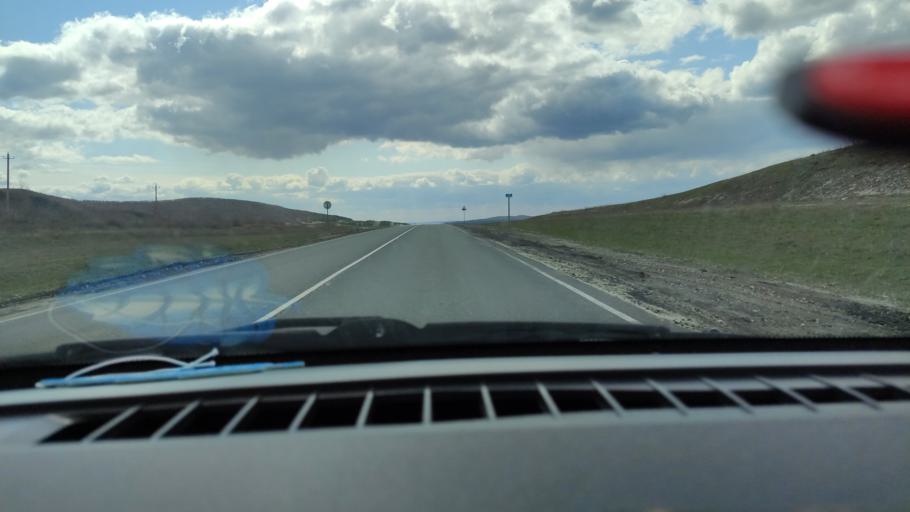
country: RU
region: Saratov
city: Alekseyevka
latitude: 52.3162
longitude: 47.9230
